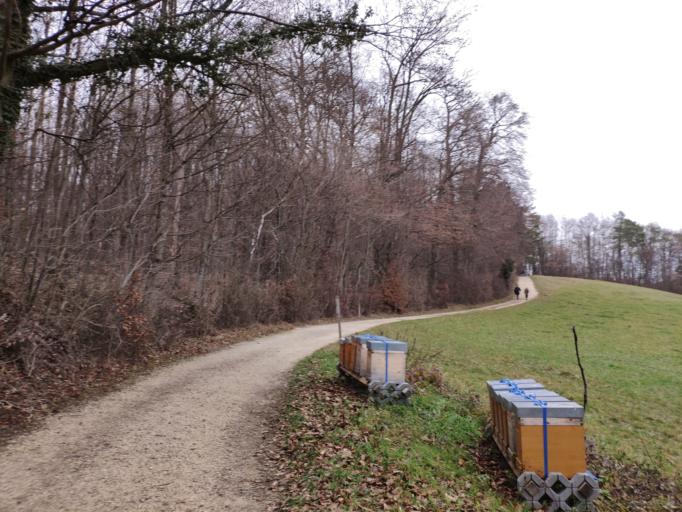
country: DE
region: Baden-Wuerttemberg
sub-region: Freiburg Region
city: Inzlingen
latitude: 47.5800
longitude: 7.6787
